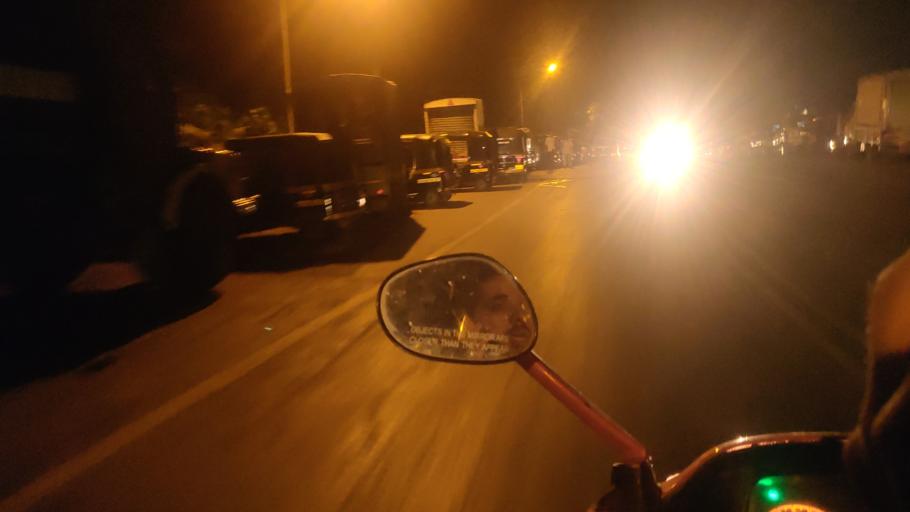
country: IN
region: Maharashtra
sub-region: Thane
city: Bhayandar
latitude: 19.2992
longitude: 72.8366
